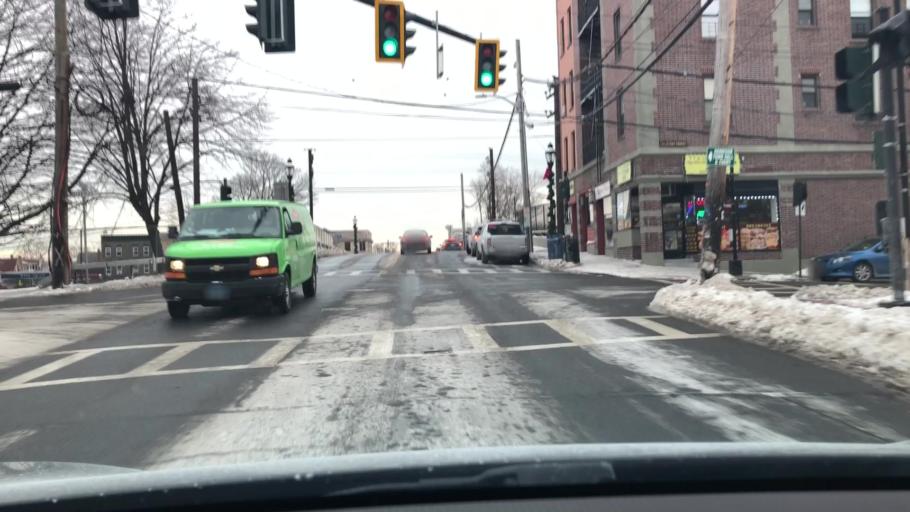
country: US
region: New York
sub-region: Westchester County
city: Harrison
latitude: 40.9701
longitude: -73.7131
